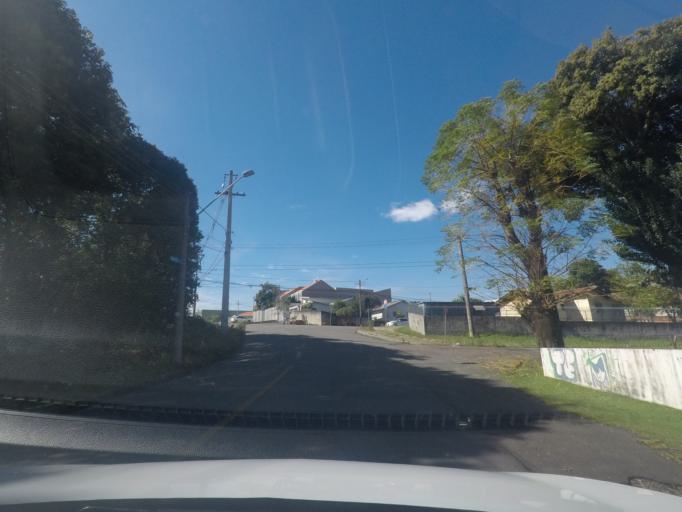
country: BR
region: Parana
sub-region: Sao Jose Dos Pinhais
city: Sao Jose dos Pinhais
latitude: -25.5049
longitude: -49.2749
